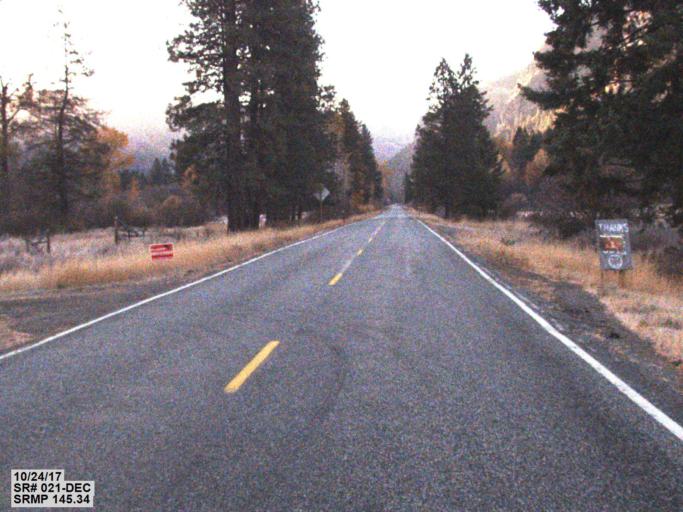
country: US
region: Washington
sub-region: Ferry County
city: Republic
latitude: 48.4550
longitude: -118.7483
